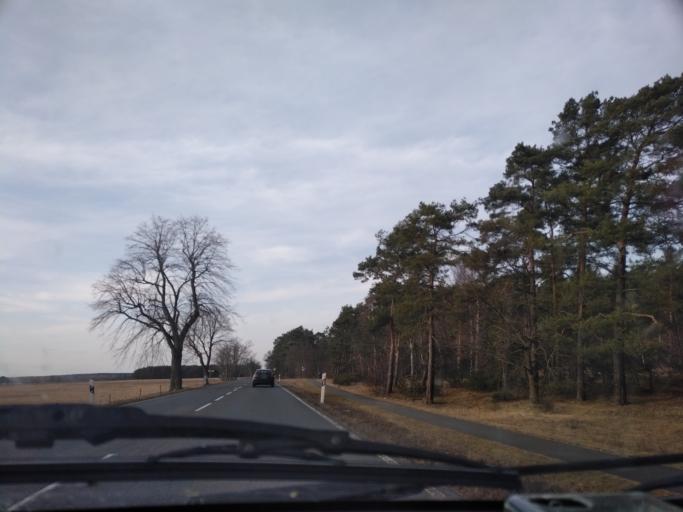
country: DE
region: Brandenburg
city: Herzberg
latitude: 51.7591
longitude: 13.2074
